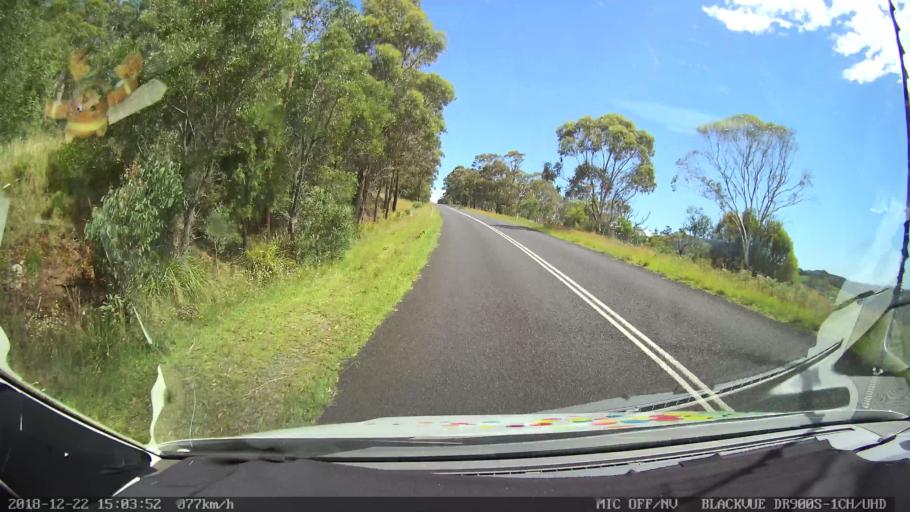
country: AU
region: New South Wales
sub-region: Bellingen
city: Dorrigo
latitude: -30.2689
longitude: 152.4386
